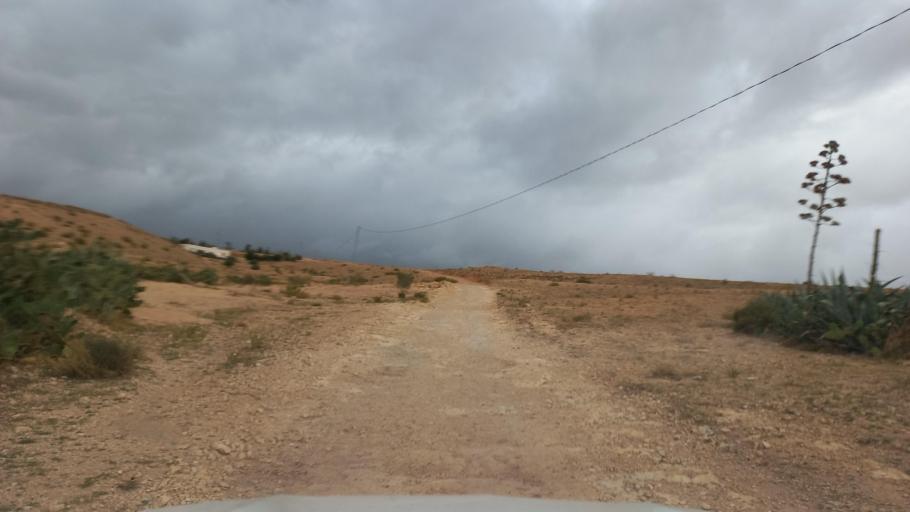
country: TN
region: Al Qasrayn
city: Kasserine
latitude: 35.2763
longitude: 8.9390
